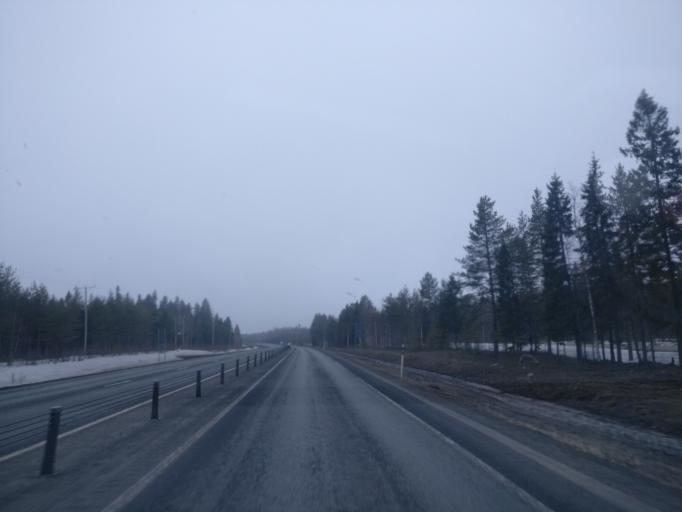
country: FI
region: Lapland
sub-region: Kemi-Tornio
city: Simo
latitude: 65.6674
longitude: 24.9748
